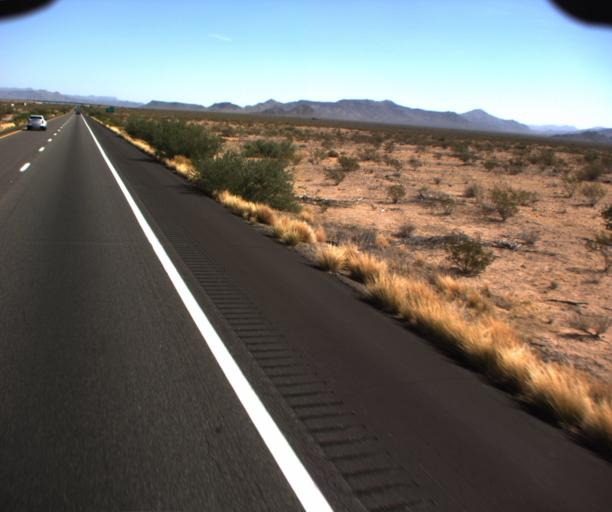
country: US
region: Arizona
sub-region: Mohave County
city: Kingman
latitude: 35.0208
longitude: -114.1325
